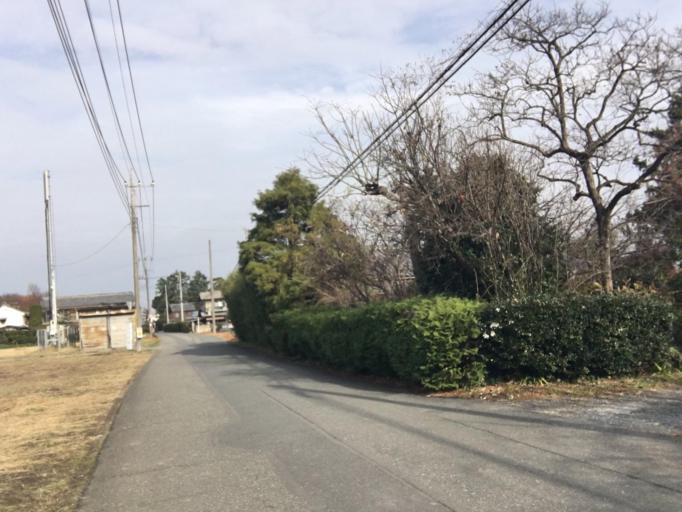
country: JP
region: Saitama
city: Yorii
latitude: 36.1386
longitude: 139.1999
